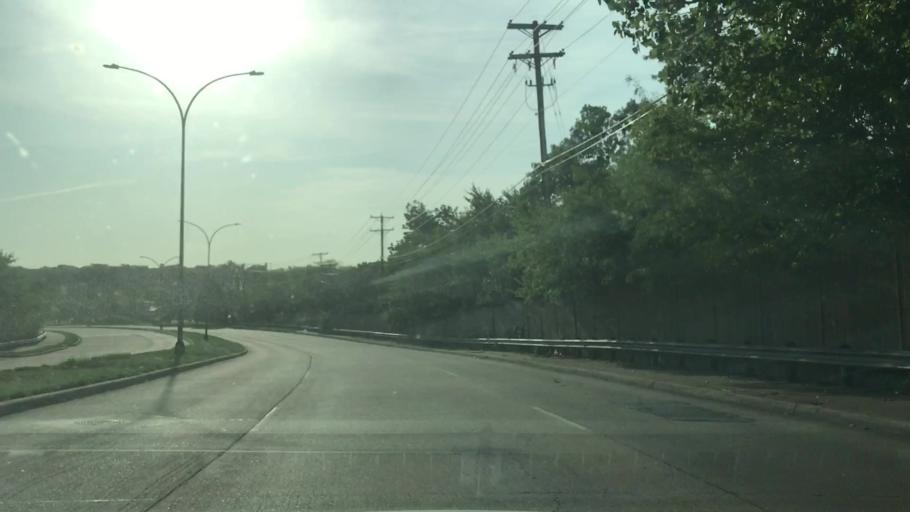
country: US
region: Texas
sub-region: Tarrant County
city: Pantego
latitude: 32.7567
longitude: -97.1531
